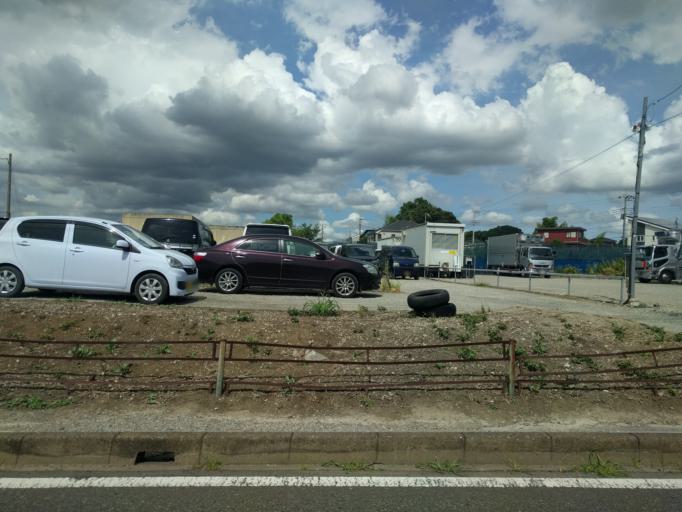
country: JP
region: Chiba
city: Funabashi
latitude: 35.7461
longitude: 139.9592
